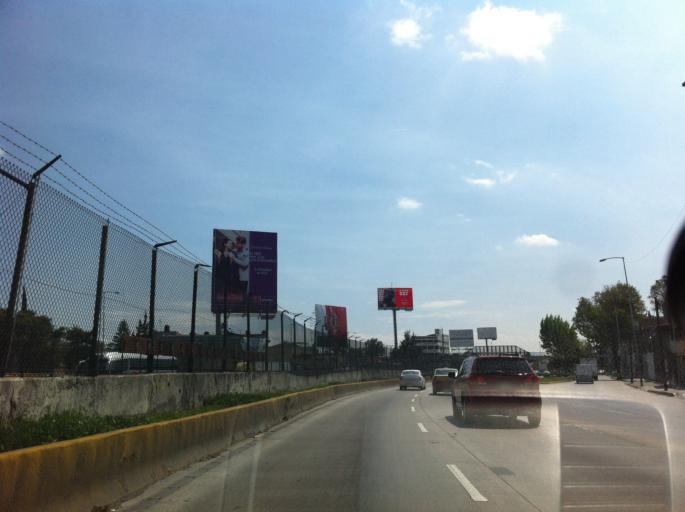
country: MX
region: Mexico City
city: Venustiano Carranza
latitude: 19.4584
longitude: -99.1183
